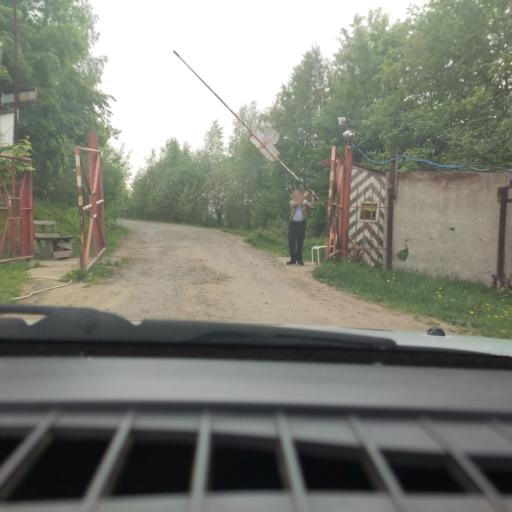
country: RU
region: Perm
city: Novyye Lyady
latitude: 57.8921
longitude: 56.6601
